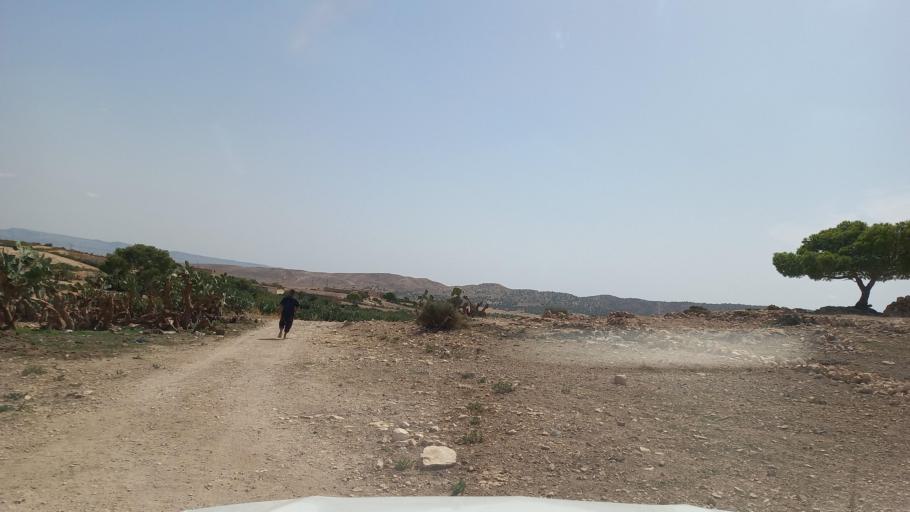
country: TN
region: Al Qasrayn
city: Sbiba
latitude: 35.4050
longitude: 8.9727
